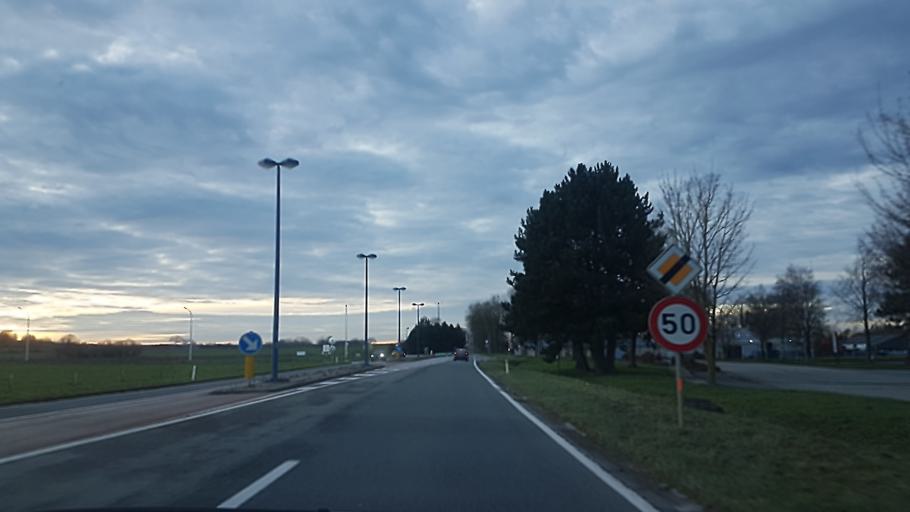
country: BE
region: Wallonia
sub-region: Province du Hainaut
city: Chimay
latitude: 50.0355
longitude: 4.3784
